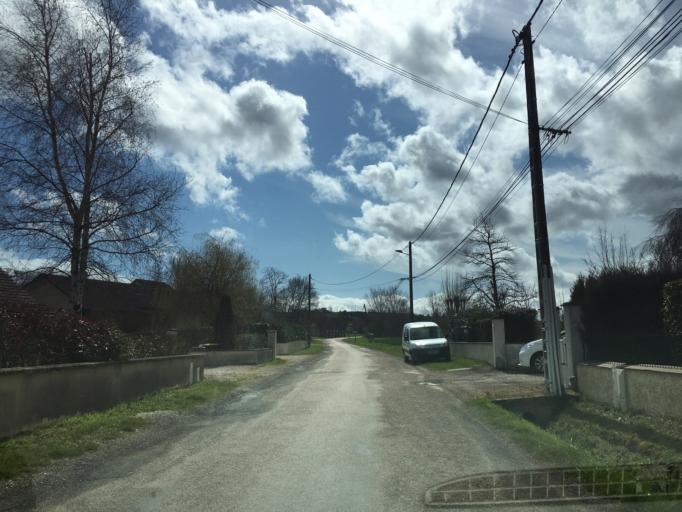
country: FR
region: Bourgogne
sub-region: Departement de l'Yonne
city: Pourrain
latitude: 47.8053
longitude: 3.4191
